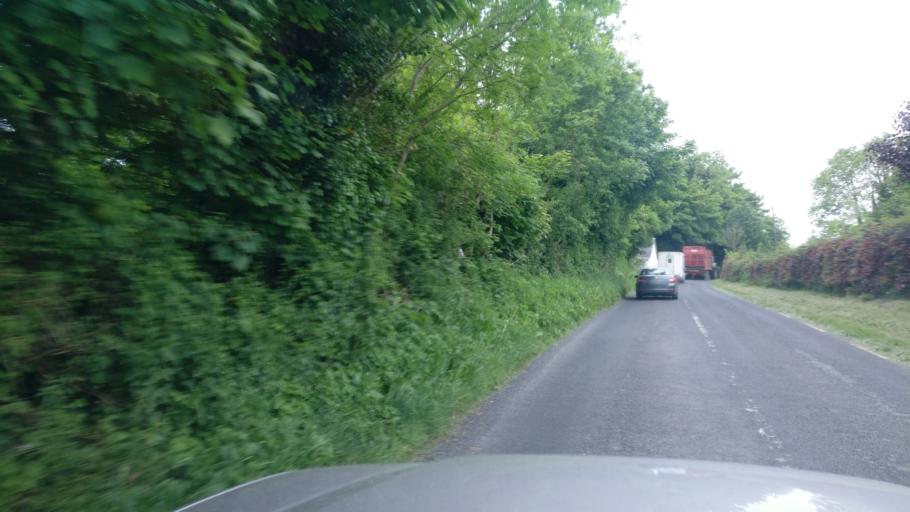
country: IE
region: Connaught
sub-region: County Galway
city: Portumna
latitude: 53.1195
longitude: -8.3155
